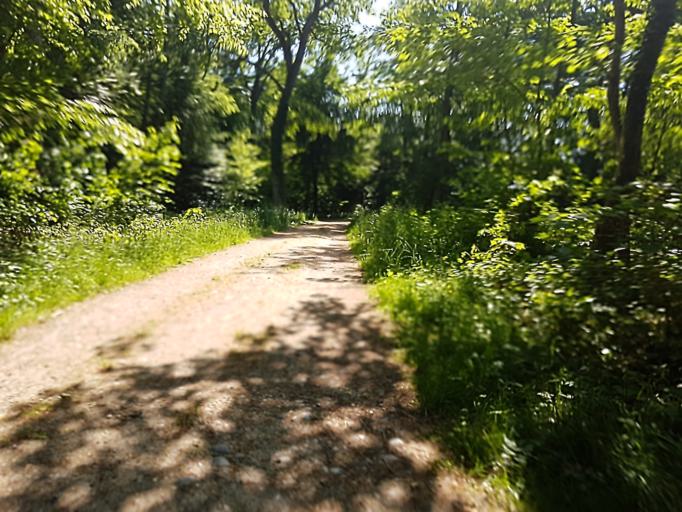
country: CH
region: Thurgau
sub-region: Arbon District
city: Amriswil
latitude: 47.5706
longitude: 9.3037
